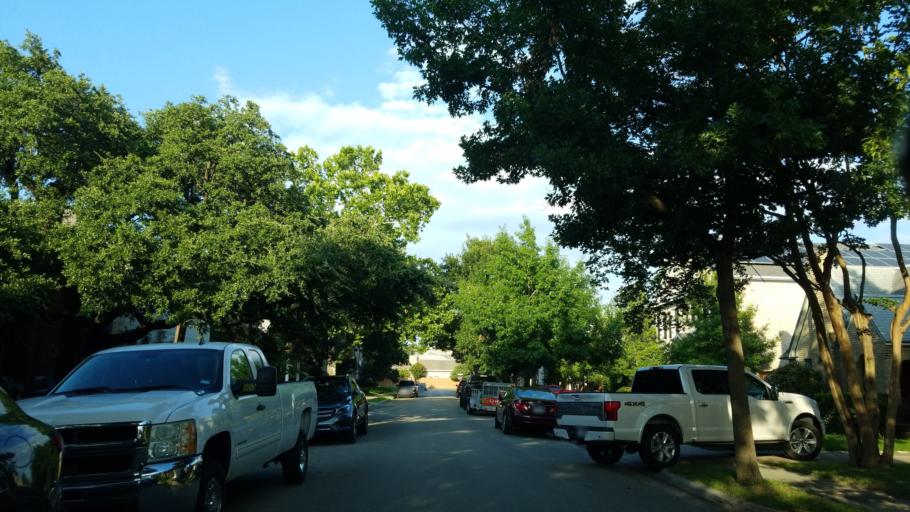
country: US
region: Texas
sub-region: Dallas County
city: Highland Park
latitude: 32.8420
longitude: -96.7936
